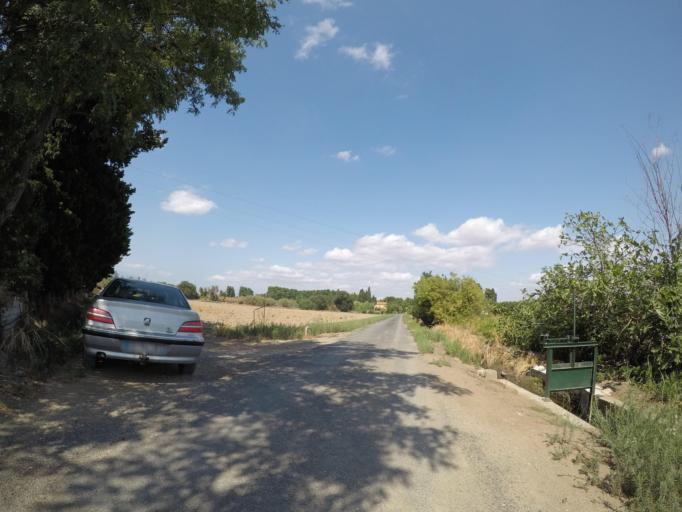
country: FR
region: Languedoc-Roussillon
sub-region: Departement des Pyrenees-Orientales
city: Saint-Esteve
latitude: 42.7009
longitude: 2.8564
